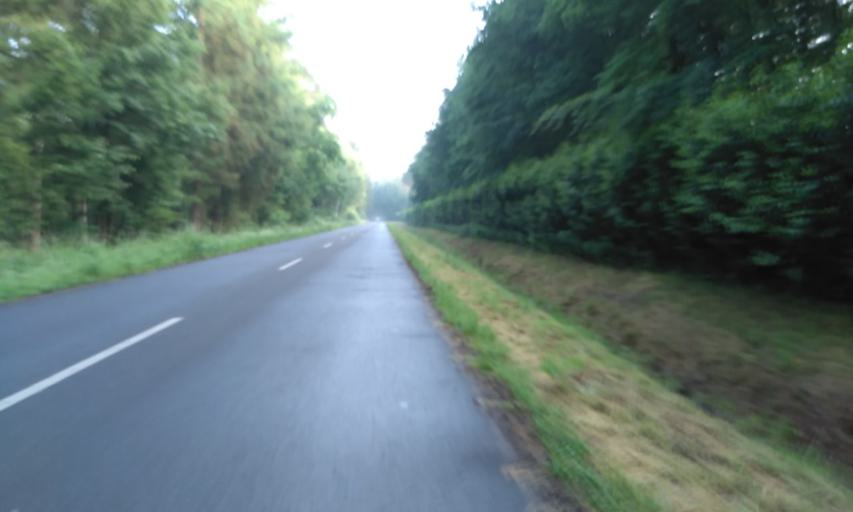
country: DE
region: Lower Saxony
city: Bargstedt
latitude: 53.4964
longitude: 9.4587
